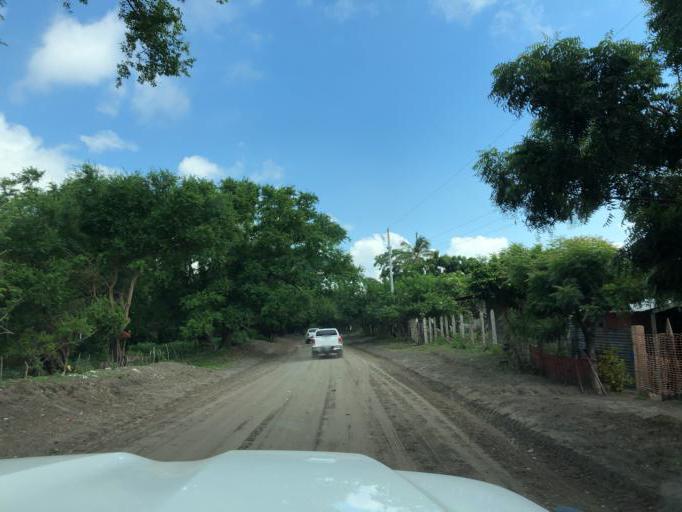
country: NI
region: Granada
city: Granada
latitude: 12.0008
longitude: -85.9351
